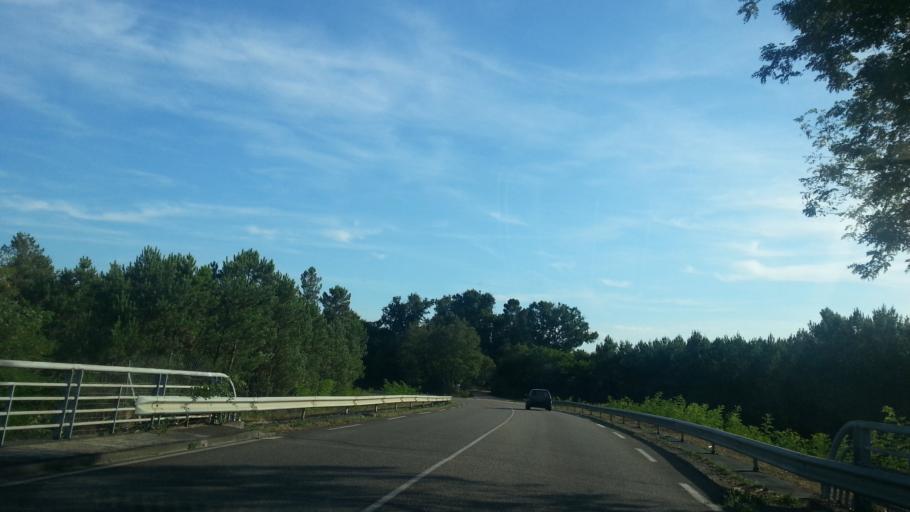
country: FR
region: Aquitaine
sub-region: Departement de la Gironde
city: Illats
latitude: 44.6084
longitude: -0.3739
